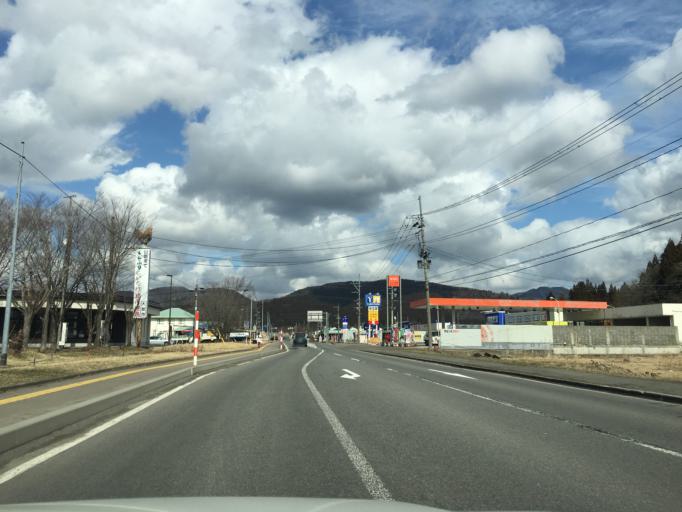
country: JP
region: Akita
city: Odate
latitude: 40.2192
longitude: 140.5859
